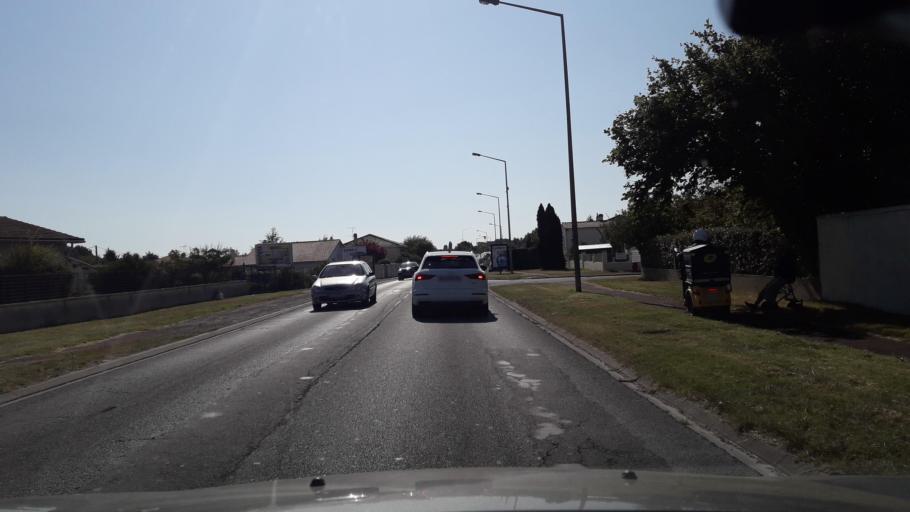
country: FR
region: Poitou-Charentes
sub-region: Departement de la Charente-Maritime
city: Saujon
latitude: 45.6749
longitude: -0.9450
